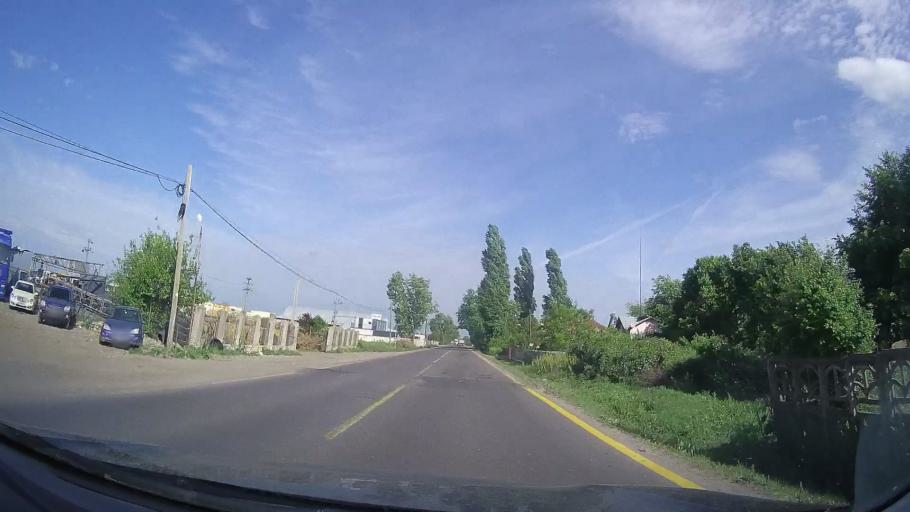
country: RO
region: Ilfov
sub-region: Comuna Magurele
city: Magurele
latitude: 44.3681
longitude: 26.0153
